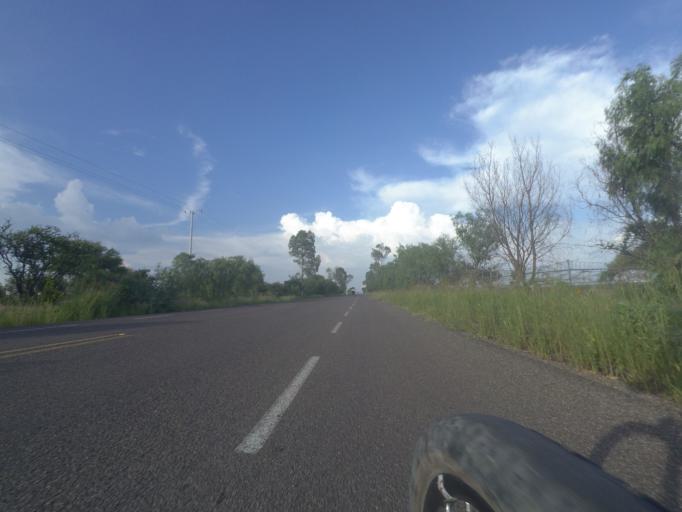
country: MX
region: Aguascalientes
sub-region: Aguascalientes
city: Penuelas (El Cienegal)
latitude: 21.7334
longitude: -102.3564
